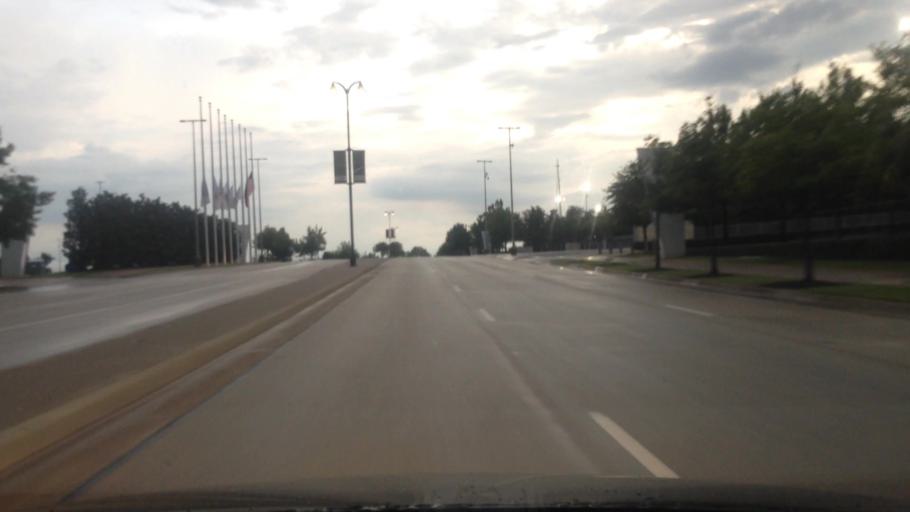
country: US
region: Texas
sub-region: Tarrant County
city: Arlington
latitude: 32.7500
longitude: -97.0896
